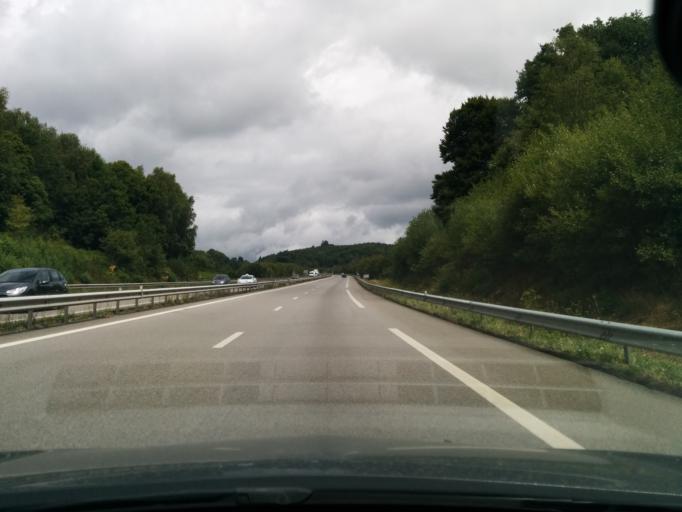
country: FR
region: Limousin
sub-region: Departement de la Haute-Vienne
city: Razes
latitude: 46.0414
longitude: 1.3510
